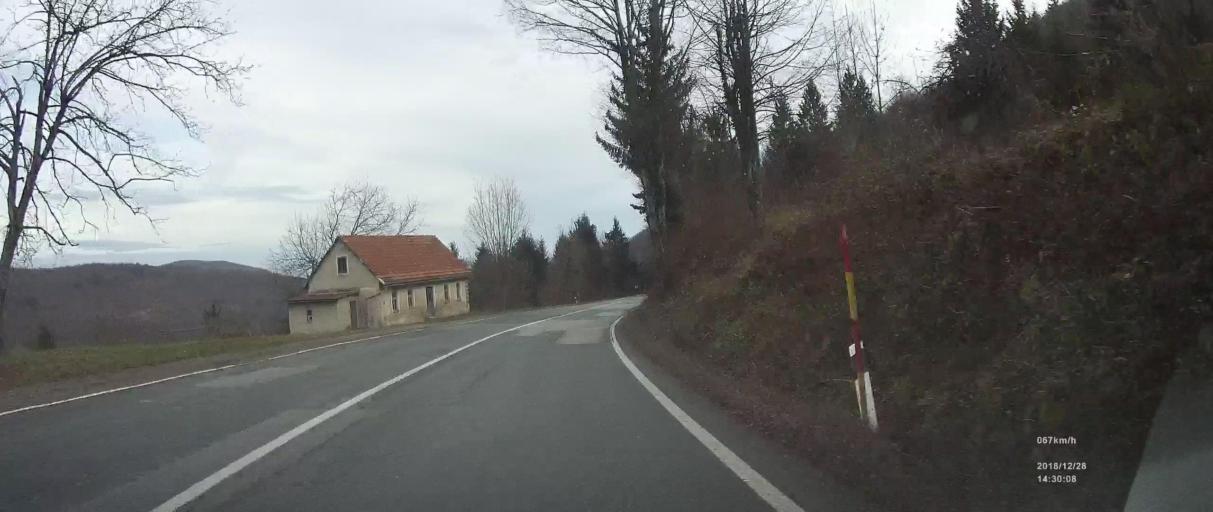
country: HR
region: Primorsko-Goranska
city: Vrbovsko
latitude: 45.4194
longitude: 15.1250
